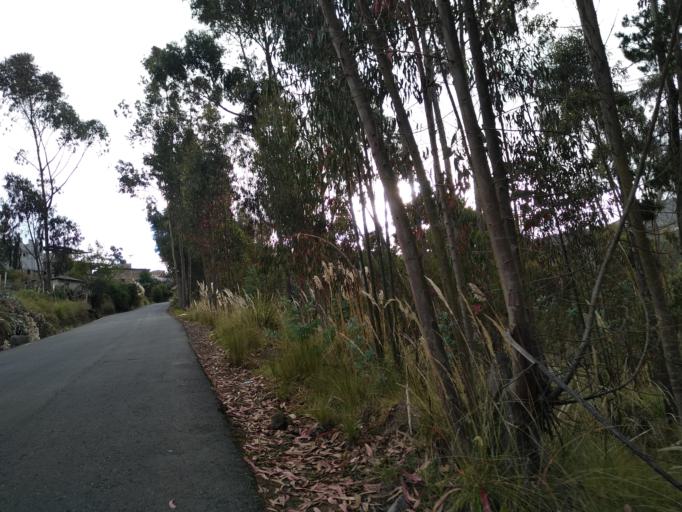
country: EC
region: Chimborazo
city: Riobamba
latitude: -1.7050
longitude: -78.7007
